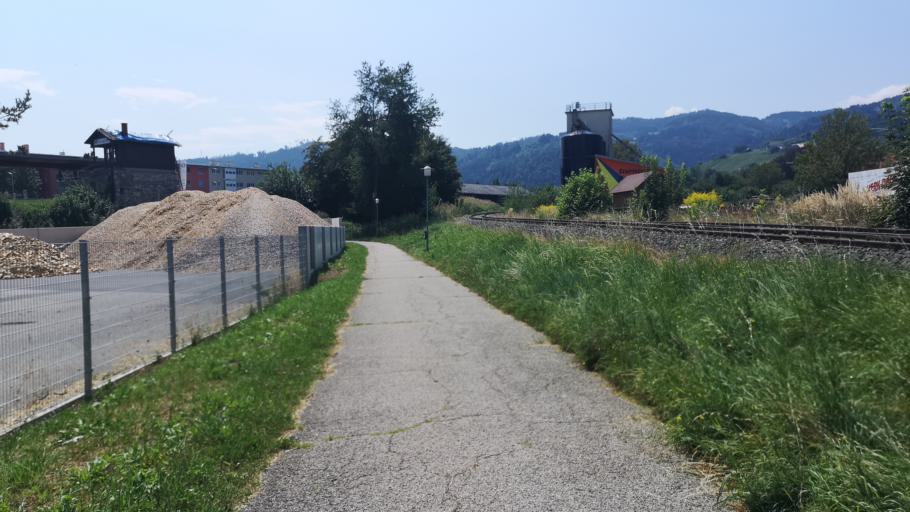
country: AT
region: Styria
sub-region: Politischer Bezirk Deutschlandsberg
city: Deutschlandsberg
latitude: 46.8197
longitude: 15.2181
